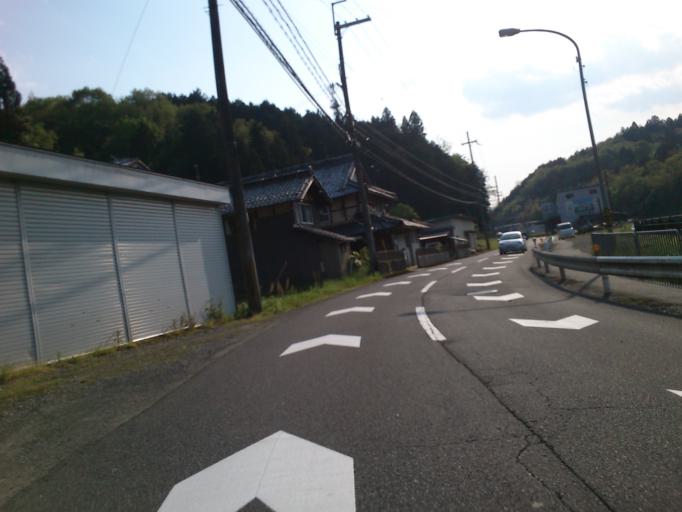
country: JP
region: Kyoto
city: Fukuchiyama
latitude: 35.2900
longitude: 135.0729
